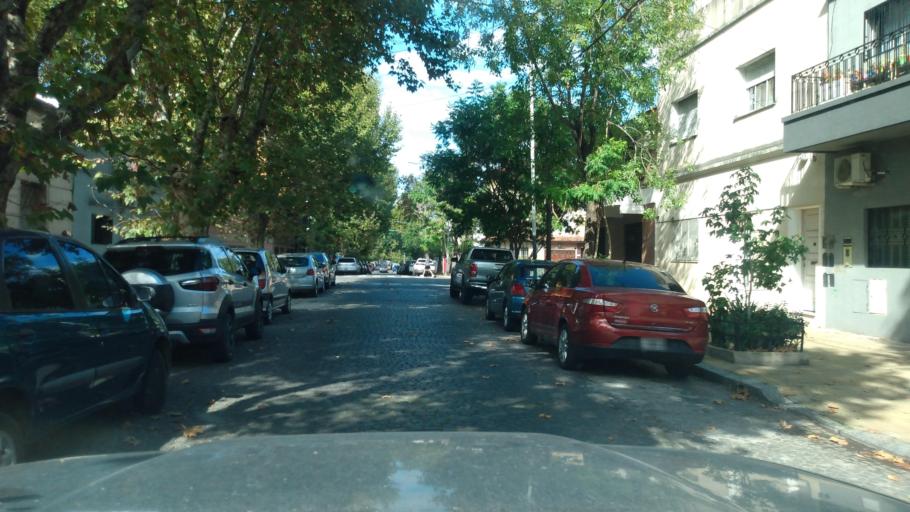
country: AR
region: Buenos Aires
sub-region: Partido de General San Martin
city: General San Martin
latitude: -34.5664
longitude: -58.4977
